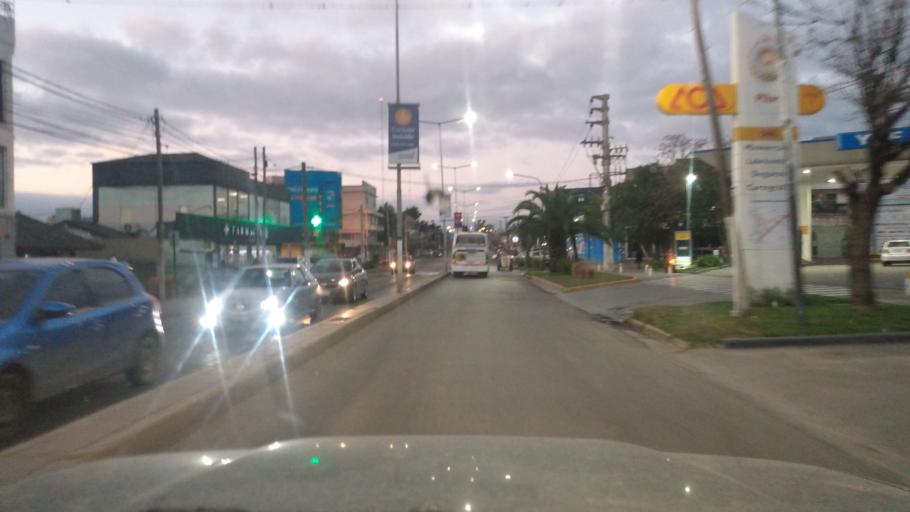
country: AR
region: Buenos Aires
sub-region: Partido de Pilar
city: Pilar
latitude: -34.4540
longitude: -58.9091
